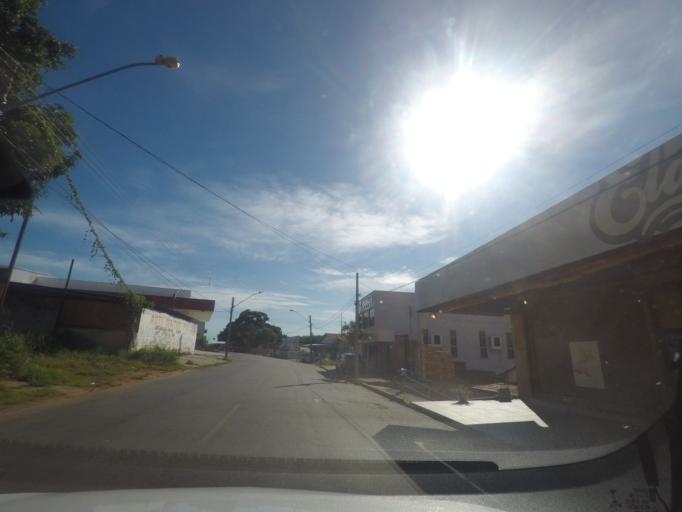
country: BR
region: Goias
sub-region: Goiania
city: Goiania
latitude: -16.6661
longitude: -49.2729
